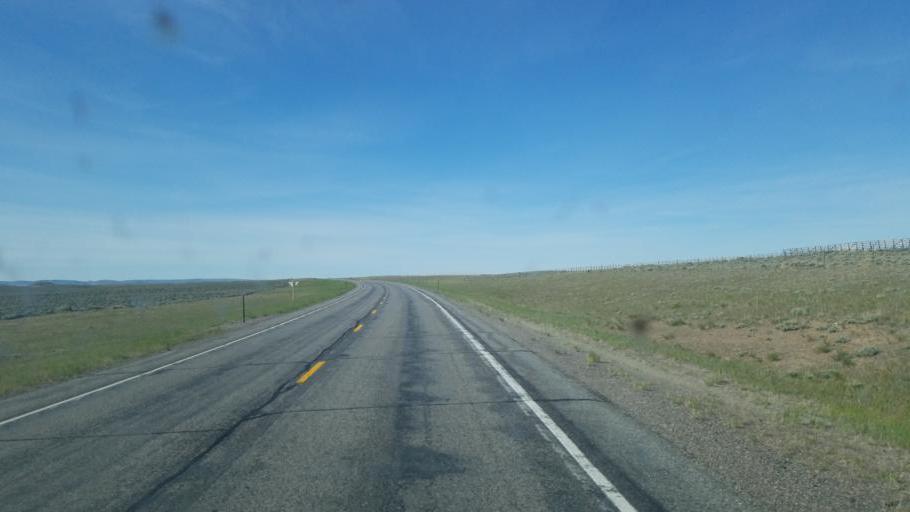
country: US
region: Wyoming
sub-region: Fremont County
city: Riverton
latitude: 42.6466
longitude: -108.1932
